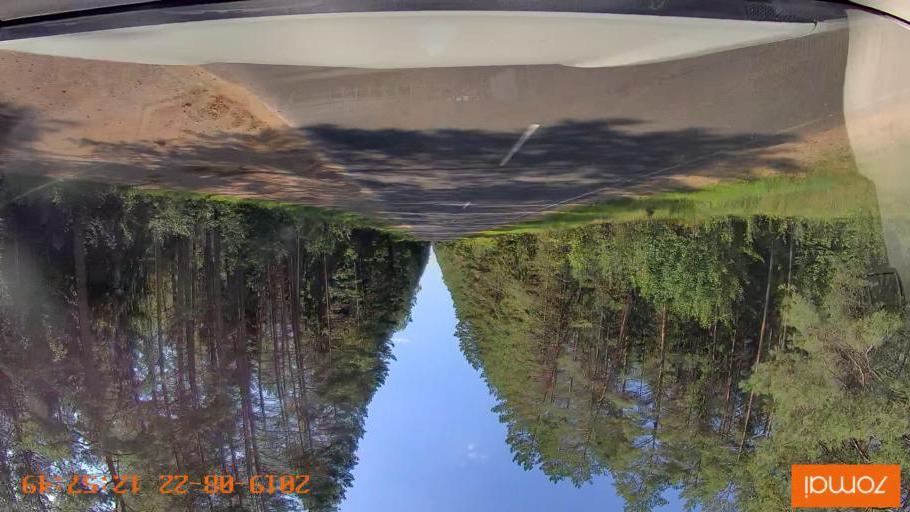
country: BY
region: Minsk
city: Prawdzinski
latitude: 53.4272
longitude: 27.7566
